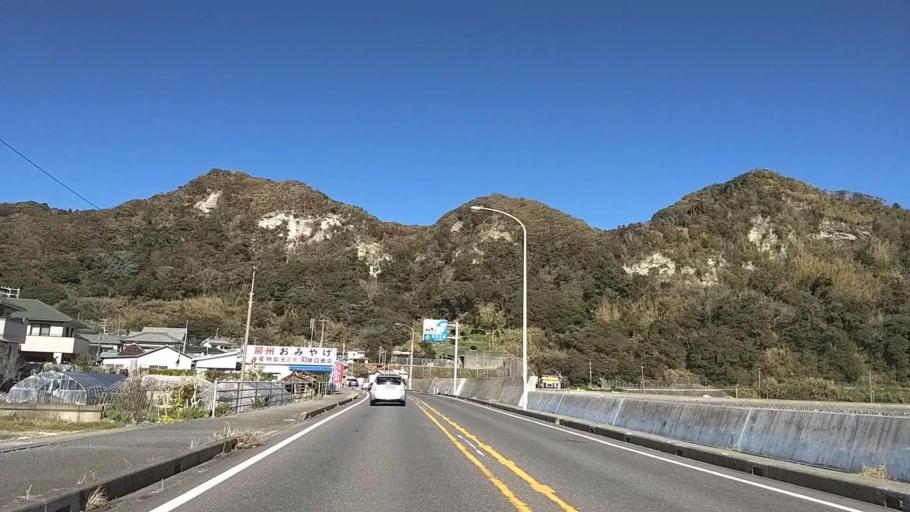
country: JP
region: Chiba
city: Kawaguchi
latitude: 35.0717
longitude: 140.0844
